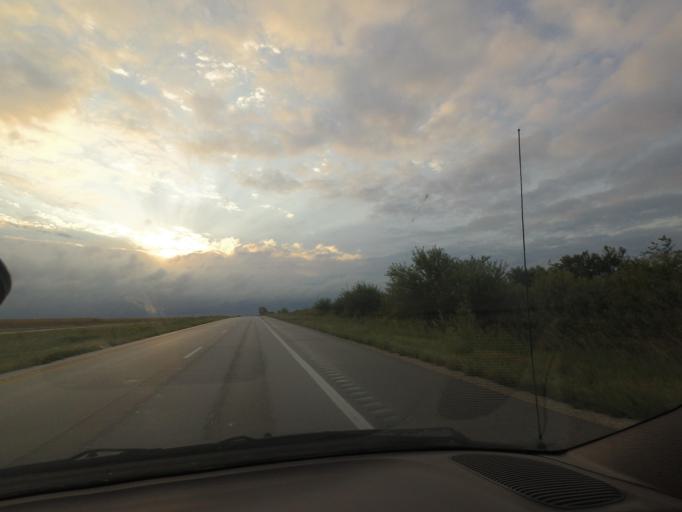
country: US
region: Missouri
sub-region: Shelby County
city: Shelbina
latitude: 39.6852
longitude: -92.0039
